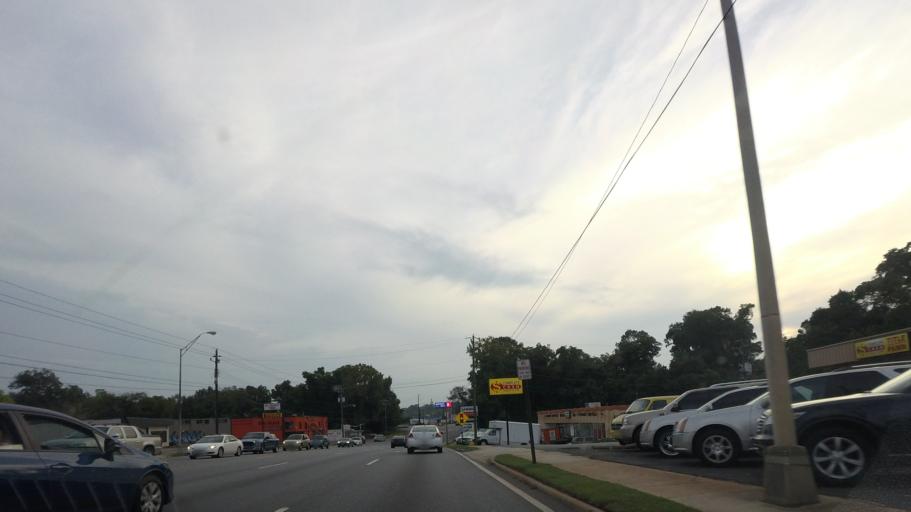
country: US
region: Georgia
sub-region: Bibb County
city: Macon
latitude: 32.8508
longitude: -83.6216
